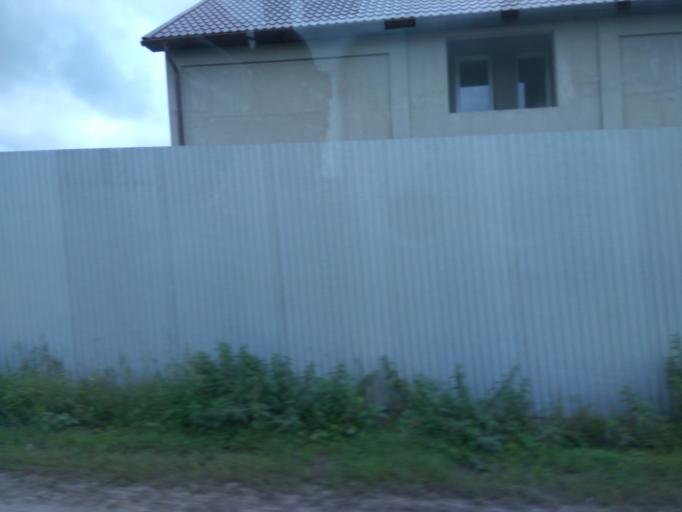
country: RU
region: Moskovskaya
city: Malyshevo
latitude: 55.5010
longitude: 38.3415
